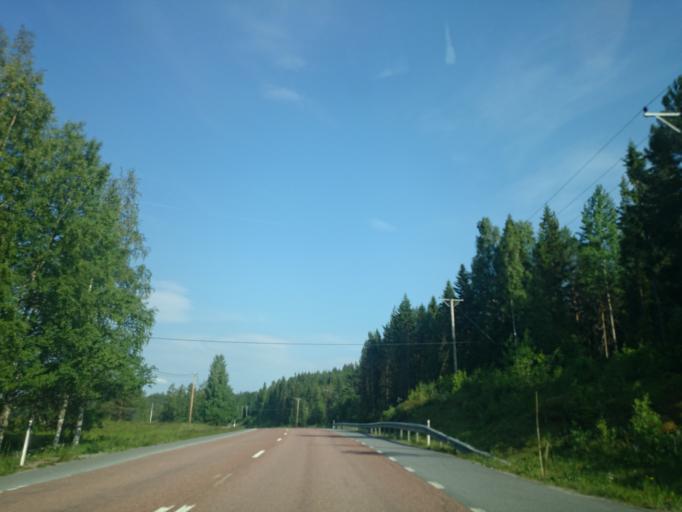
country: SE
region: Jaemtland
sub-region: OEstersunds Kommun
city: Brunflo
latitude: 62.9542
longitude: 15.1386
